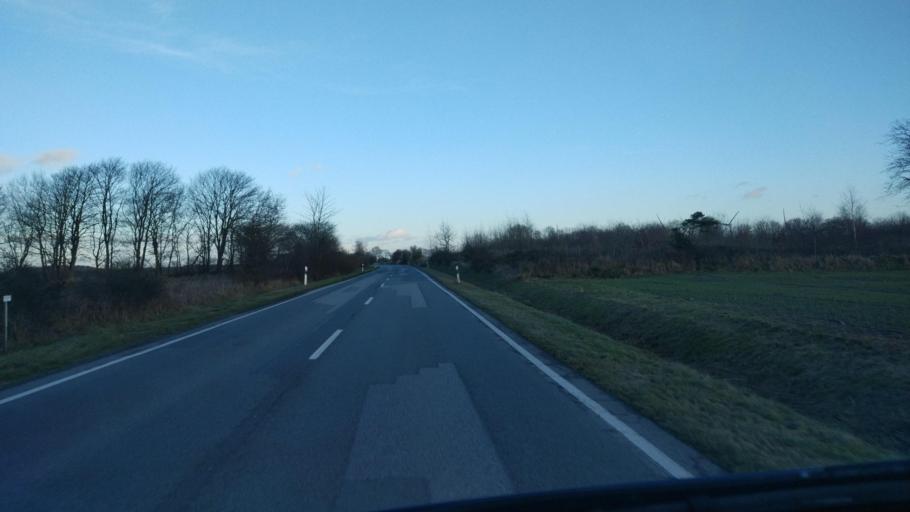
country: DE
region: Schleswig-Holstein
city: Oldersbek
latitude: 54.4616
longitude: 9.1747
